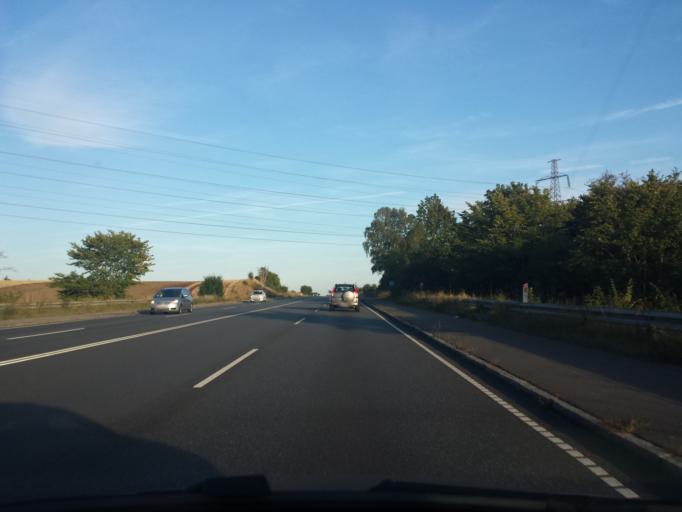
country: DK
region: Capital Region
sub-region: Egedal Kommune
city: Stenlose
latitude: 55.7659
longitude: 12.2094
